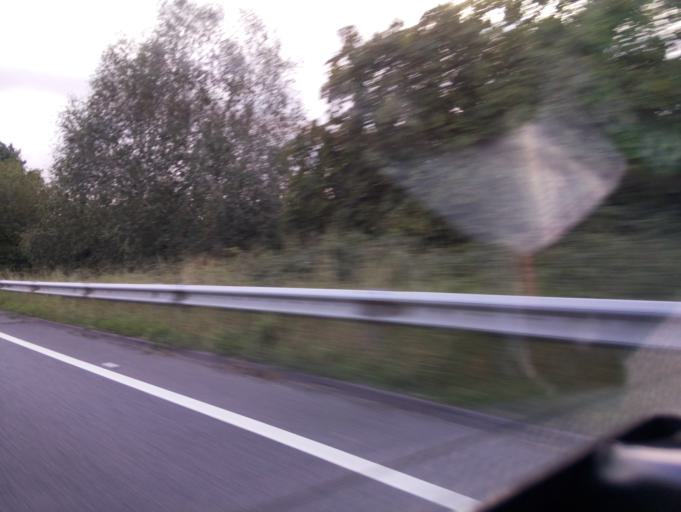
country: GB
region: England
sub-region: Somerset
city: Chard
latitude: 50.8901
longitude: -3.0584
